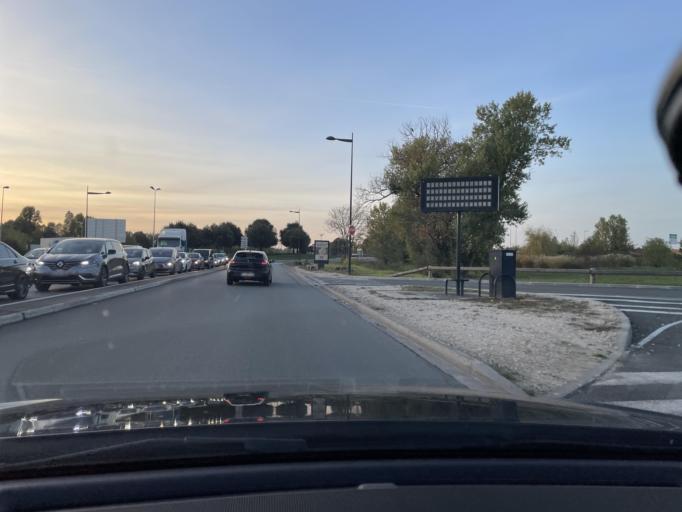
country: FR
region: Aquitaine
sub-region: Departement de la Gironde
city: Villenave-d'Ornon
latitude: 44.7915
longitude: -0.5369
